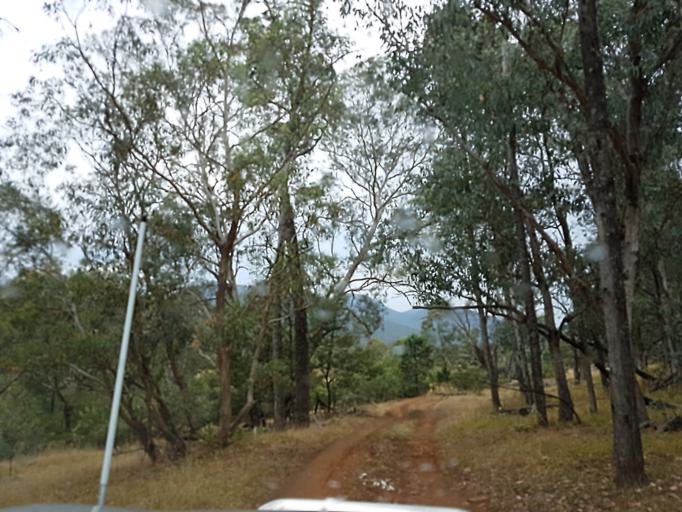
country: AU
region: New South Wales
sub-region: Snowy River
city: Jindabyne
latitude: -36.9456
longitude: 148.3956
